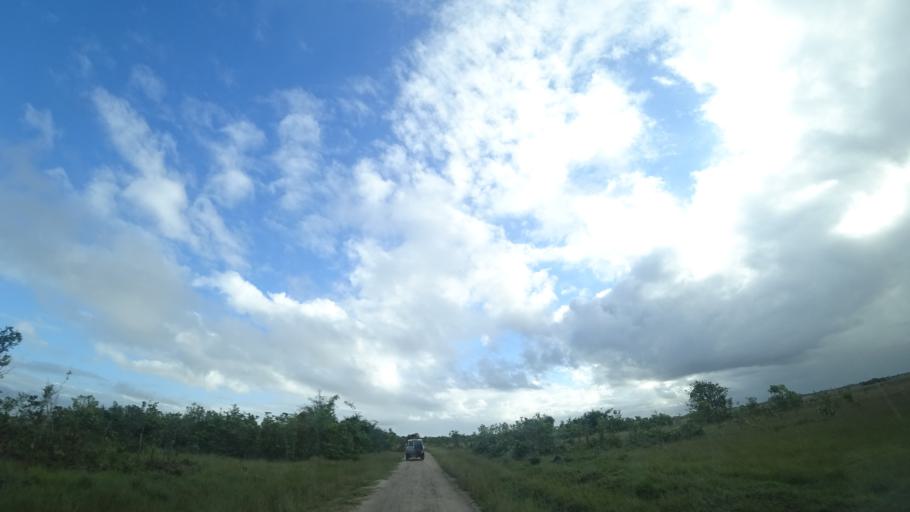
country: MZ
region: Sofala
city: Beira
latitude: -19.6694
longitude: 35.0585
